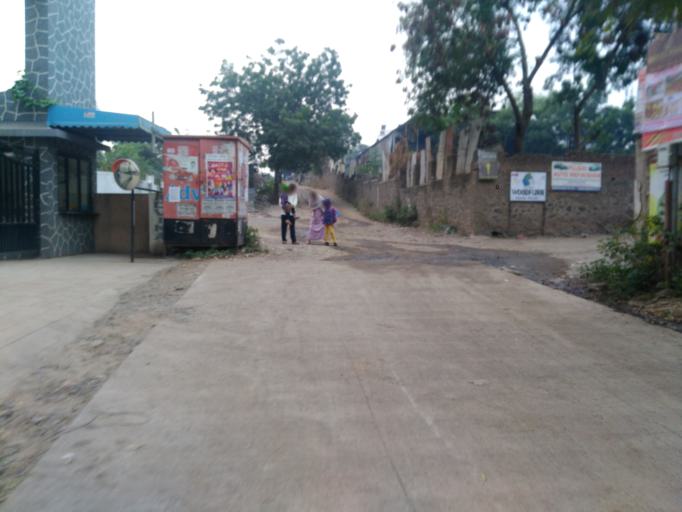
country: IN
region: Maharashtra
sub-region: Pune Division
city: Pune
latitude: 18.4458
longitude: 73.8980
